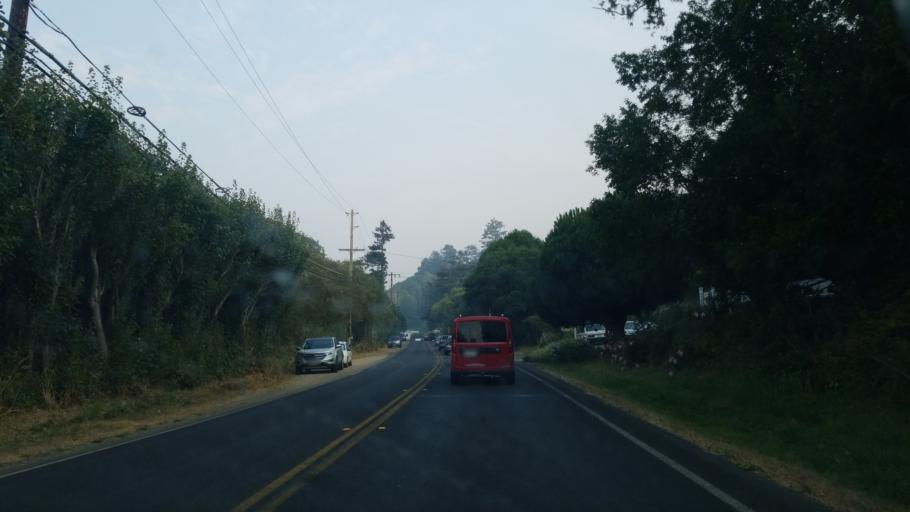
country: US
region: California
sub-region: Marin County
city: Inverness
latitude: 38.0716
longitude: -122.8263
